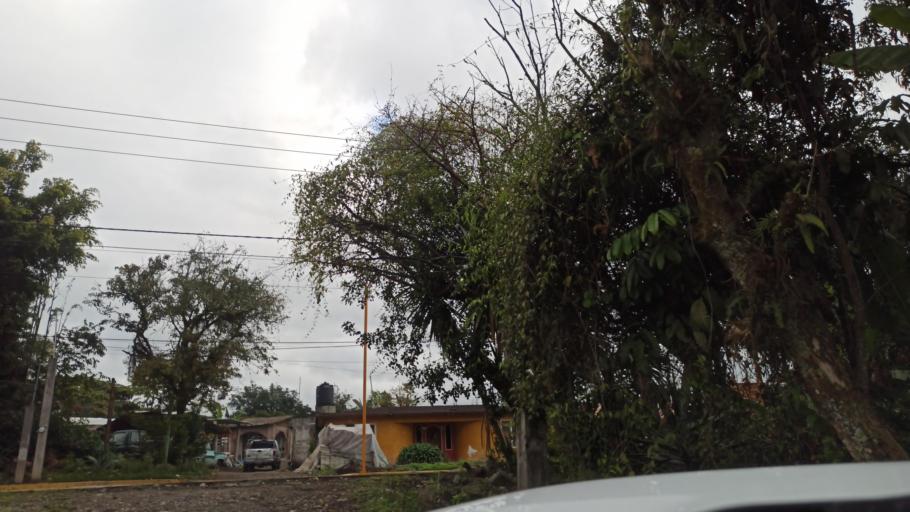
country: MX
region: Veracruz
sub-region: Chocaman
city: San Jose Neria
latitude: 19.0036
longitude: -97.0060
